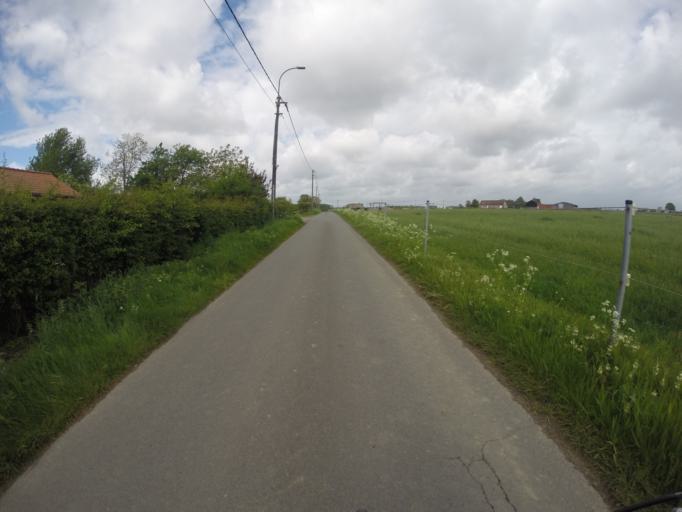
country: BE
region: Flanders
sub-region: Provincie Oost-Vlaanderen
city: Aalter
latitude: 51.0518
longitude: 3.4464
